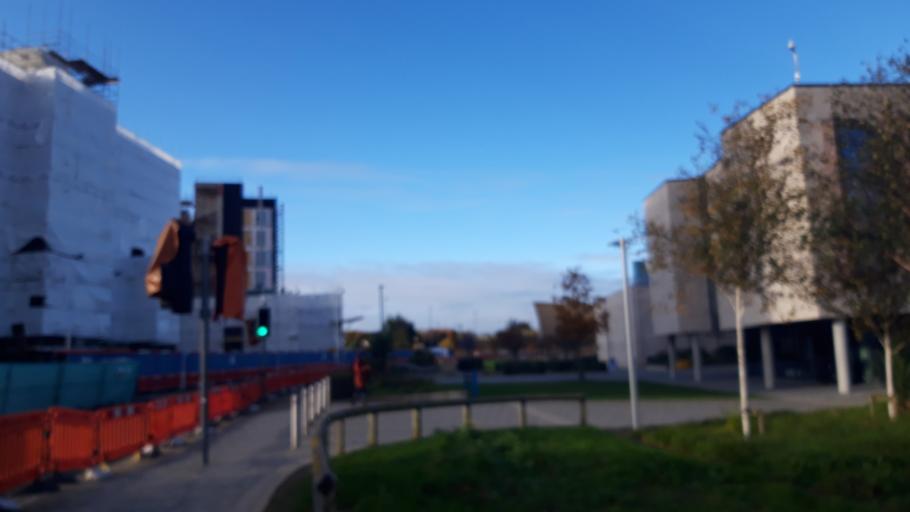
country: IE
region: Leinster
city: Mount Merrion
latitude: 53.3040
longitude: -6.2179
